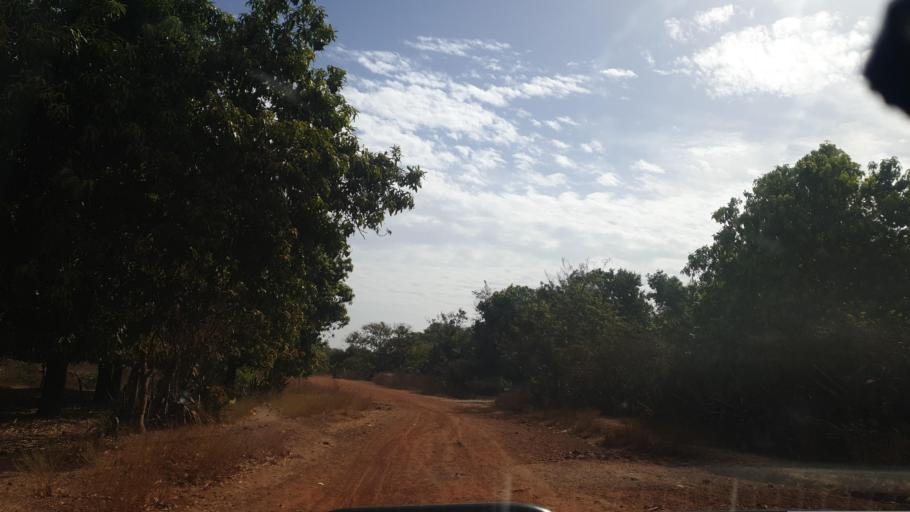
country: ML
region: Sikasso
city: Yanfolila
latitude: 11.4178
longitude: -7.9927
